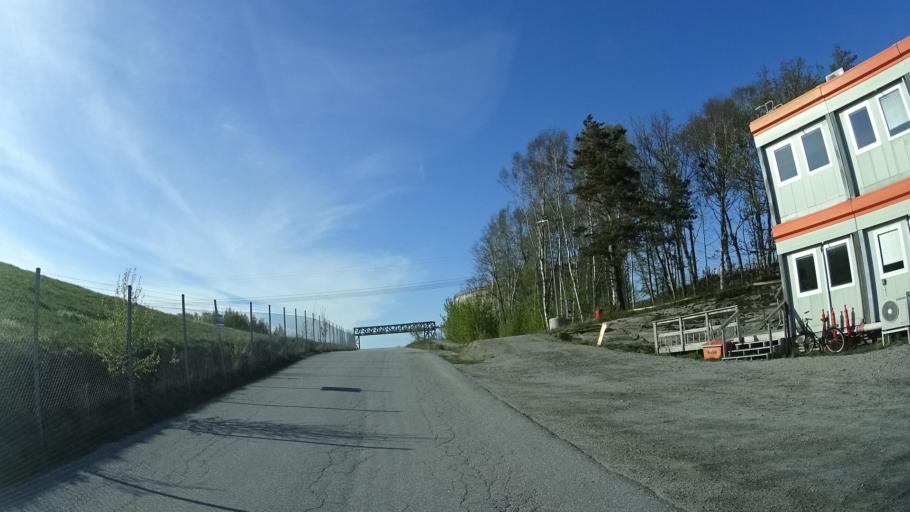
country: SE
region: Vaestra Goetaland
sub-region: Stenungsunds Kommun
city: Stenungsund
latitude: 58.0837
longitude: 11.8155
